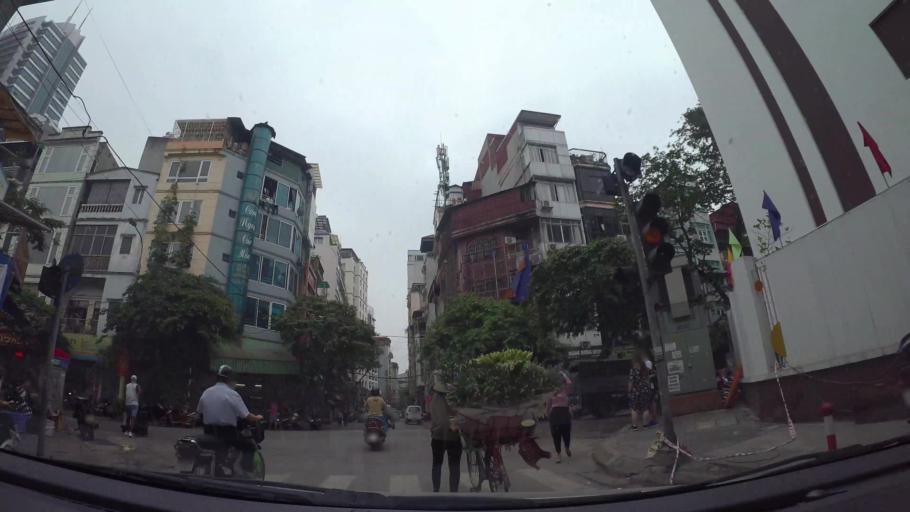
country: VN
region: Ha Noi
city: Hoan Kiem
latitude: 21.0434
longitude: 105.8434
